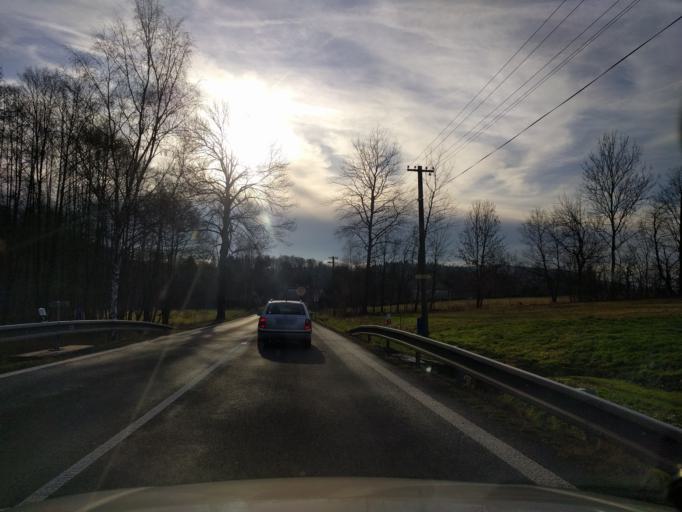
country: CZ
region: Liberecky
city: Mnisek
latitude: 50.8487
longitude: 15.0312
